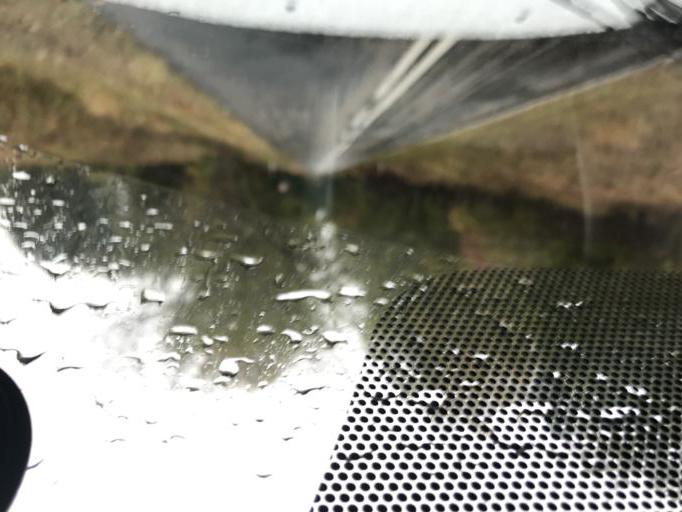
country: DE
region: Brandenburg
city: Neulewin
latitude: 52.7810
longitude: 14.2916
